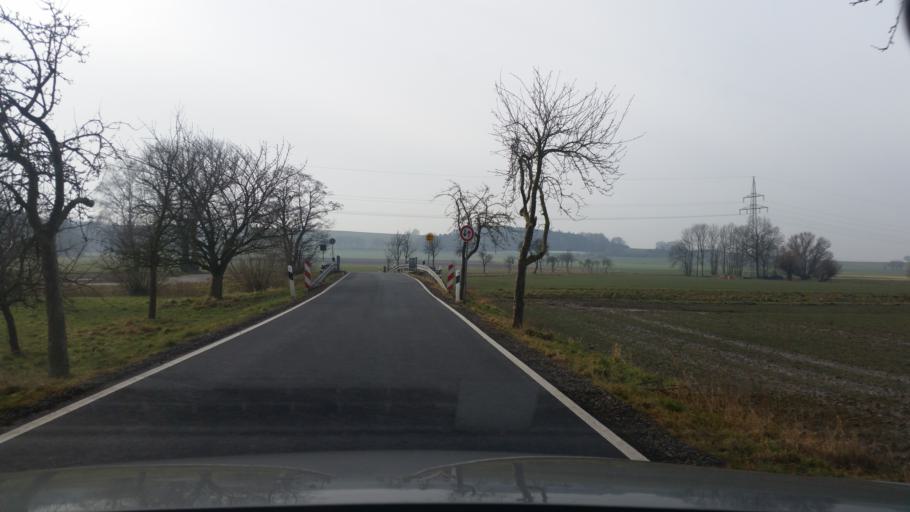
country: DE
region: Lower Saxony
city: Grossgoltern
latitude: 52.3595
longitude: 9.5349
